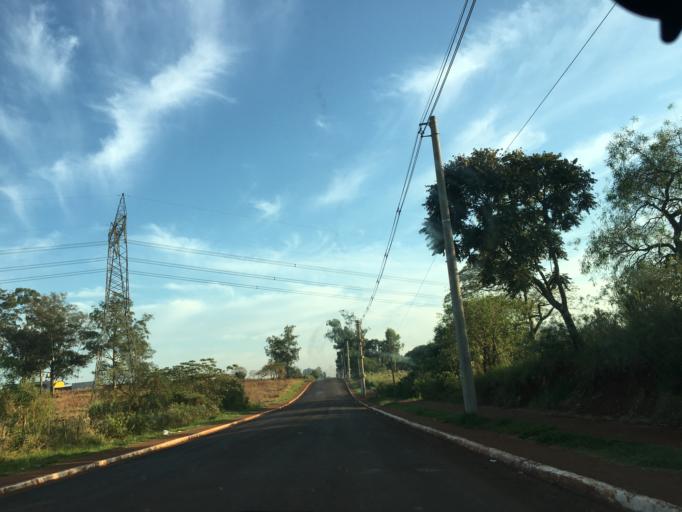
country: AR
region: Misiones
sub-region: Departamento de Capital
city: Posadas
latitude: -27.4513
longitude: -55.9340
